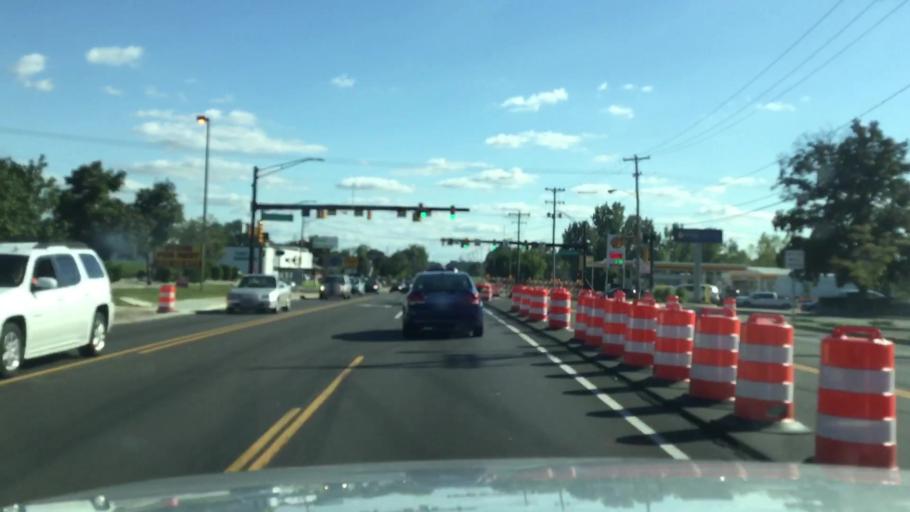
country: US
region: Michigan
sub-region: Kalamazoo County
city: Portage
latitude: 42.2164
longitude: -85.5894
